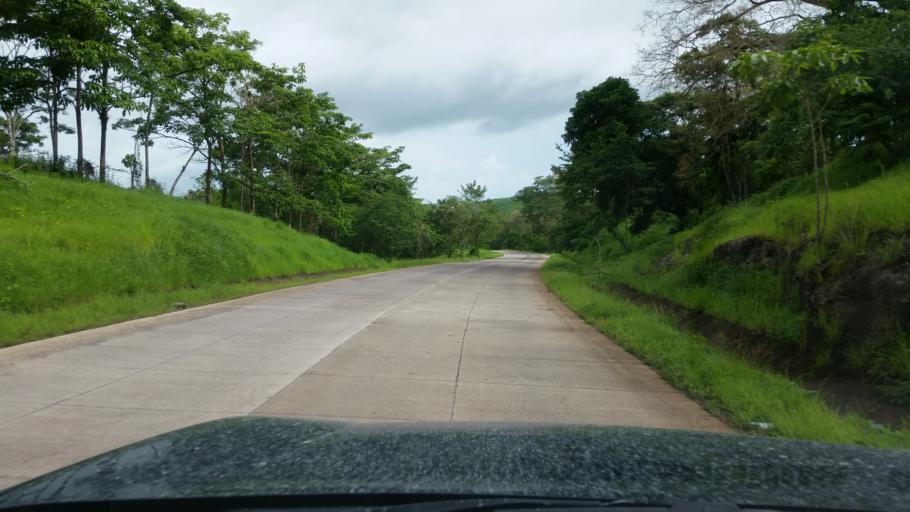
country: NI
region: Atlantico Norte (RAAN)
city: Siuna
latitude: 13.5334
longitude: -84.8230
